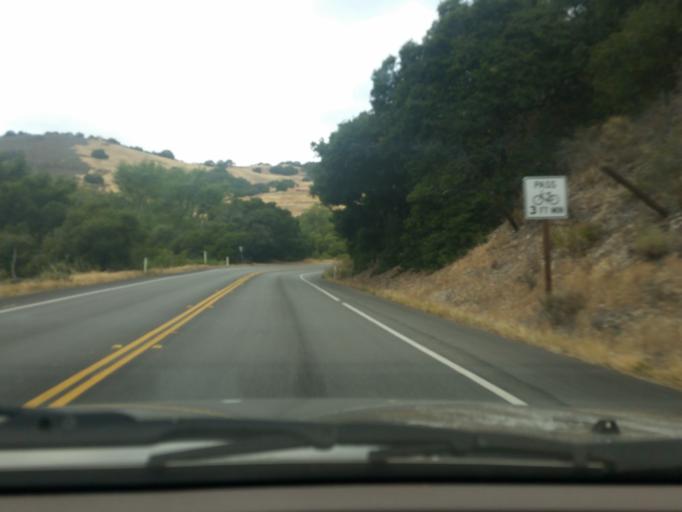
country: US
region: California
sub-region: San Luis Obispo County
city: Avila Beach
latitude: 35.1863
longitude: -120.7245
